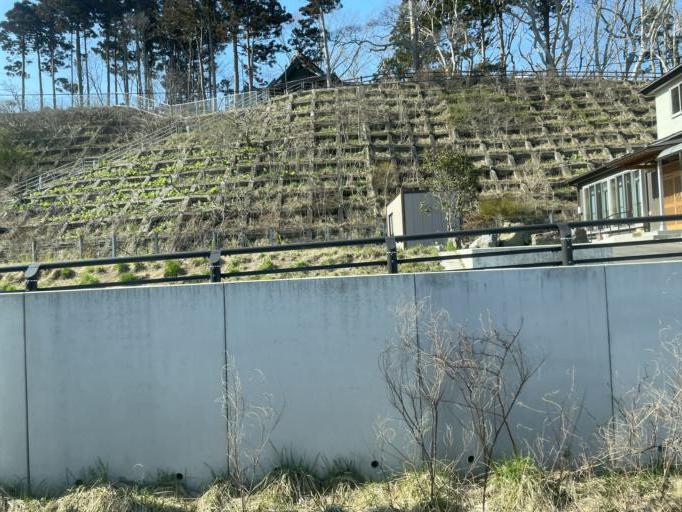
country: JP
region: Aomori
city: Hachinohe
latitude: 40.3449
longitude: 141.7683
